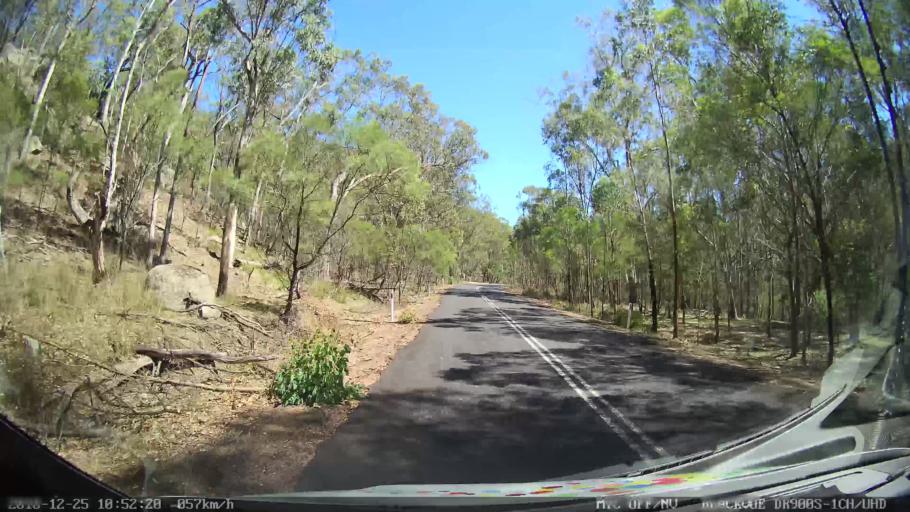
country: AU
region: New South Wales
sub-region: Upper Hunter Shire
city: Merriwa
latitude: -32.4297
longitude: 150.2735
